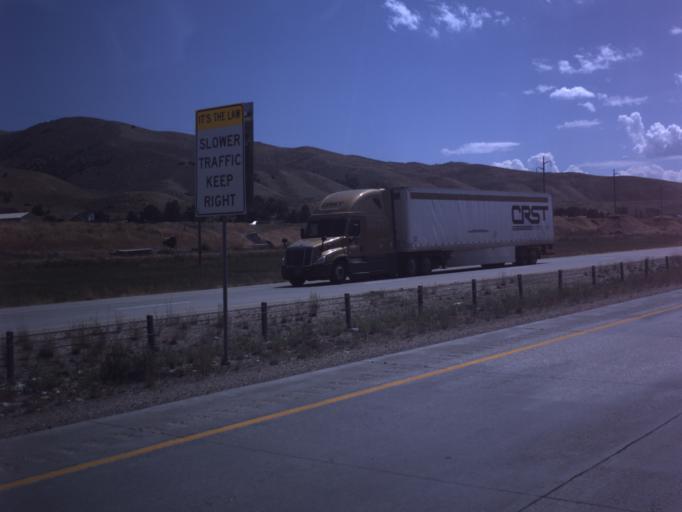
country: US
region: Utah
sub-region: Morgan County
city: Mountain Green
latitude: 41.1071
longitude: -111.7483
